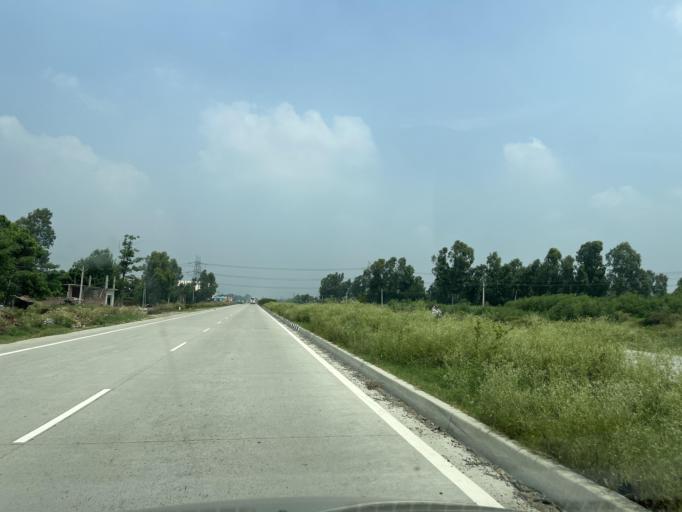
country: IN
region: Uttar Pradesh
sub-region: Bijnor
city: Najibabad
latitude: 29.5575
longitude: 78.3390
